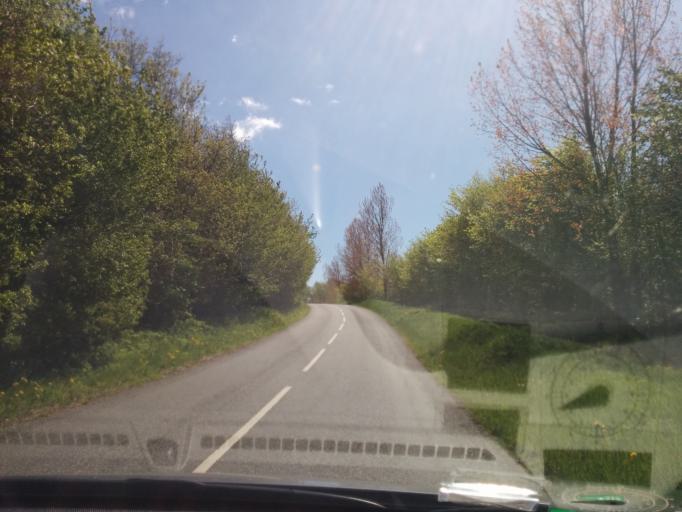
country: DK
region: Central Jutland
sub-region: Arhus Kommune
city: Framlev
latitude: 56.1222
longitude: 10.0160
